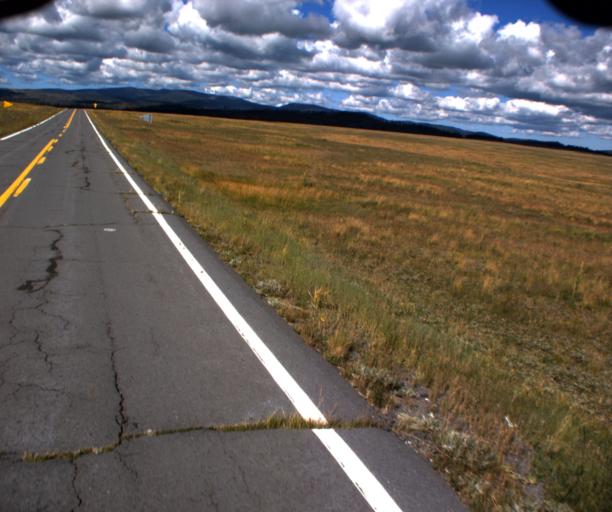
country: US
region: Arizona
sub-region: Apache County
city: Eagar
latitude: 33.9624
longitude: -109.3891
